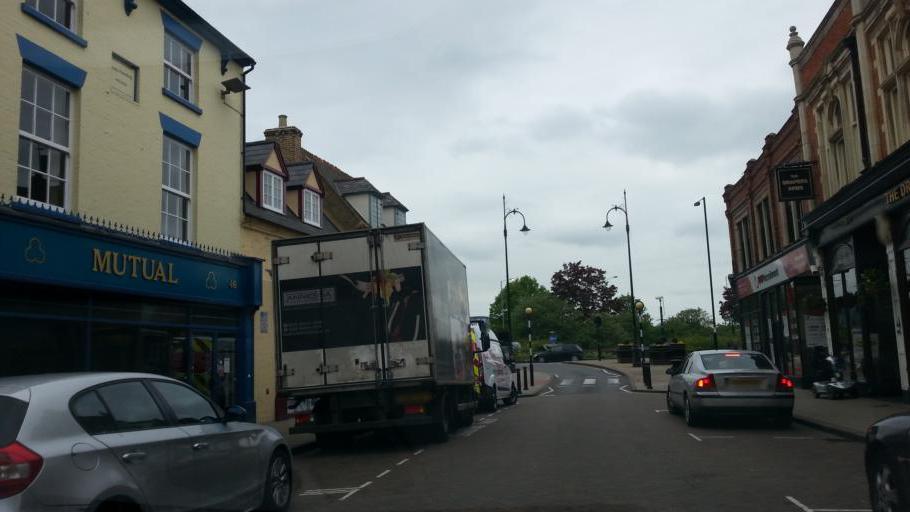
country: GB
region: England
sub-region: Peterborough
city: Peterborough
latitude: 52.5729
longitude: -0.2462
